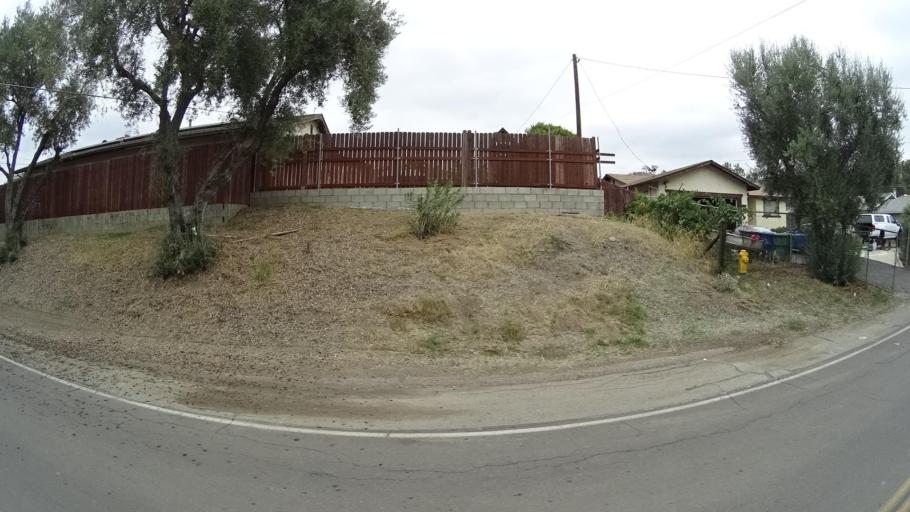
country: US
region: California
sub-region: San Diego County
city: Spring Valley
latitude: 32.7407
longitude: -116.9987
